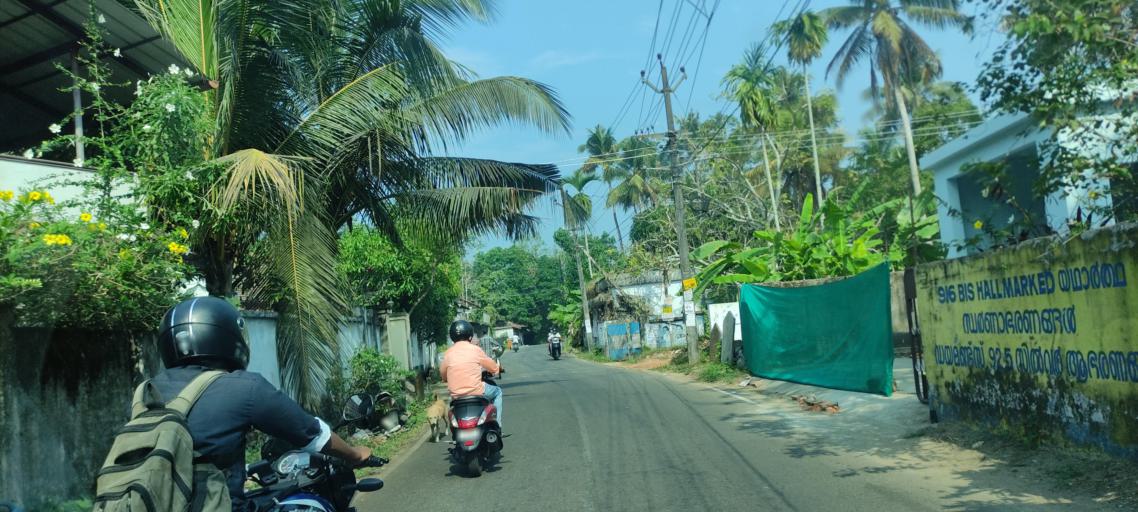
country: IN
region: Kerala
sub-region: Alappuzha
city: Kutiatodu
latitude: 9.7734
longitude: 76.3075
